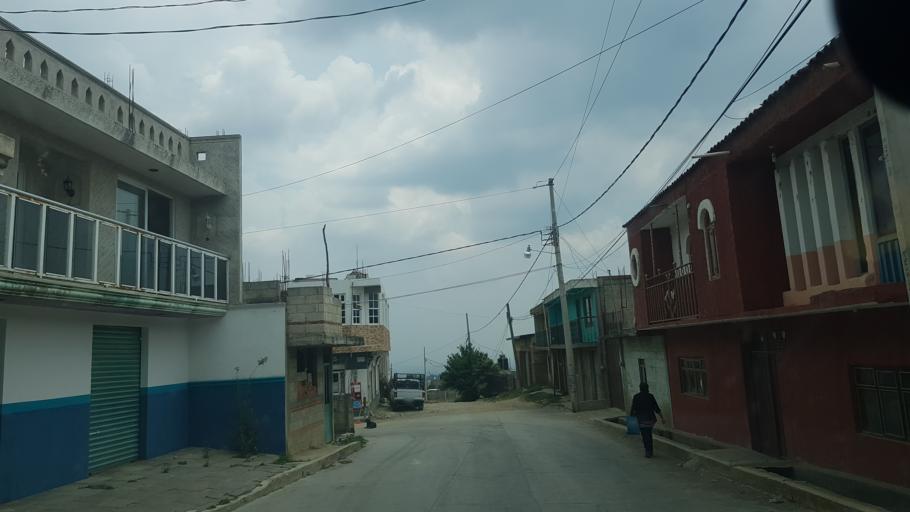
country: MX
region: Puebla
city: Domingo Arenas
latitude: 19.1505
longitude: -98.4935
